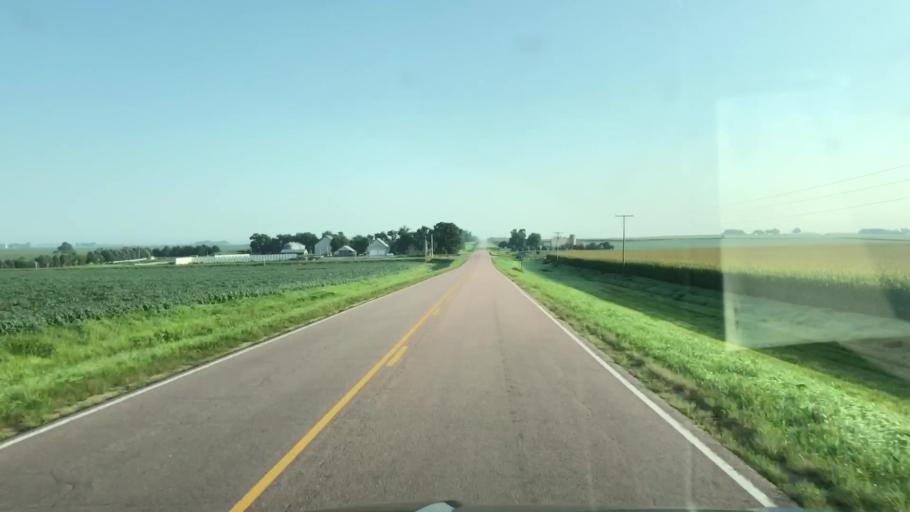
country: US
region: Iowa
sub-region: Lyon County
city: George
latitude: 43.2701
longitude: -95.9999
